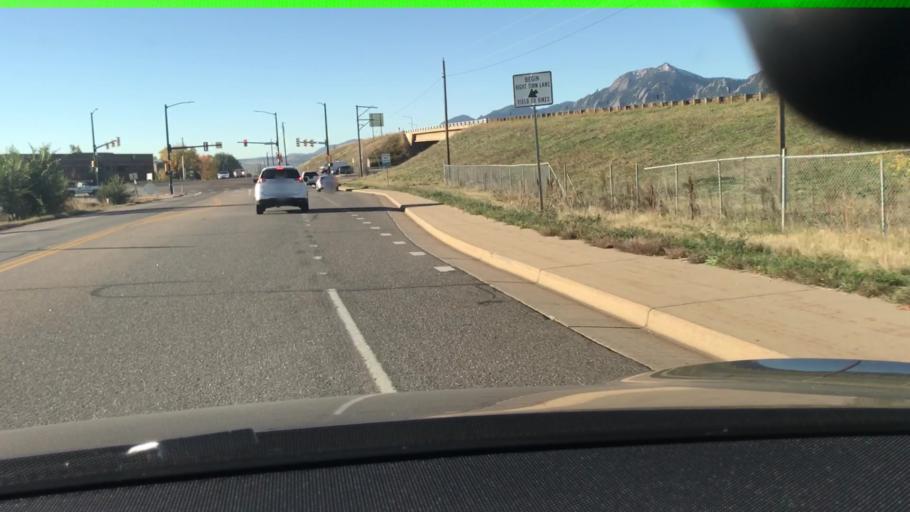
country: US
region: Colorado
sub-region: Boulder County
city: Boulder
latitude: 40.0398
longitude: -105.2442
